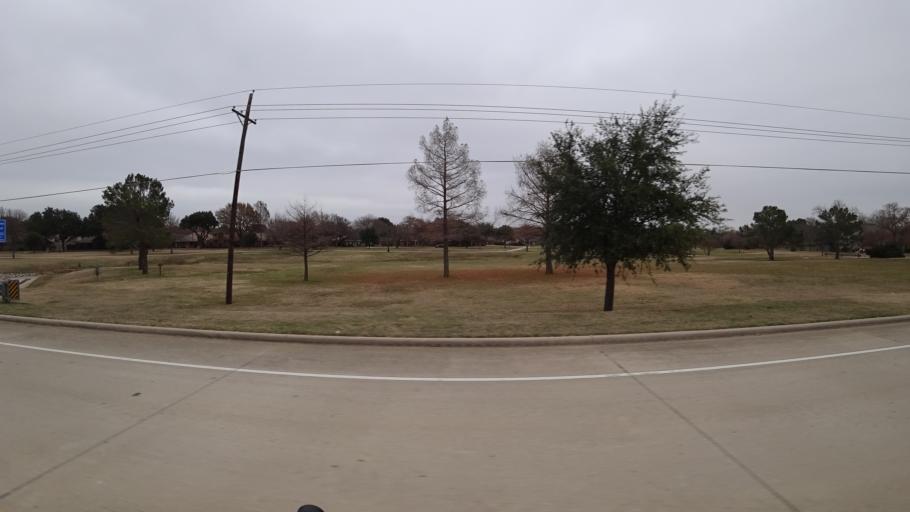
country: US
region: Texas
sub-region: Denton County
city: Highland Village
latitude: 33.0565
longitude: -97.0445
